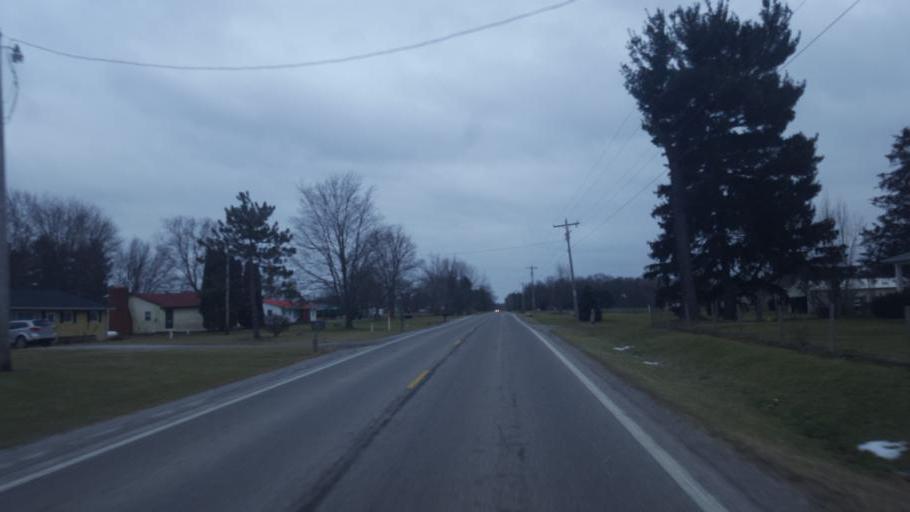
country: US
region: Ohio
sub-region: Morrow County
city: Mount Gilead
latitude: 40.5137
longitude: -82.8172
